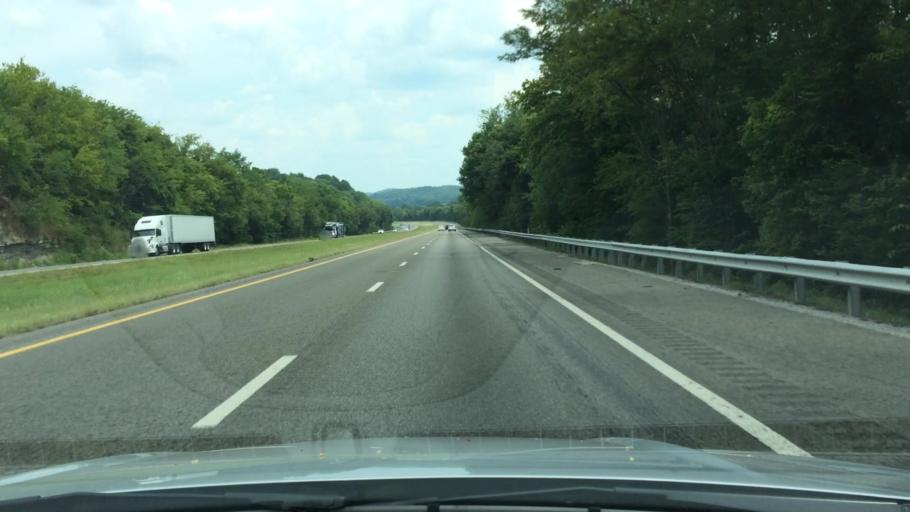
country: US
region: Tennessee
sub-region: Marshall County
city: Cornersville
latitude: 35.4077
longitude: -86.8795
